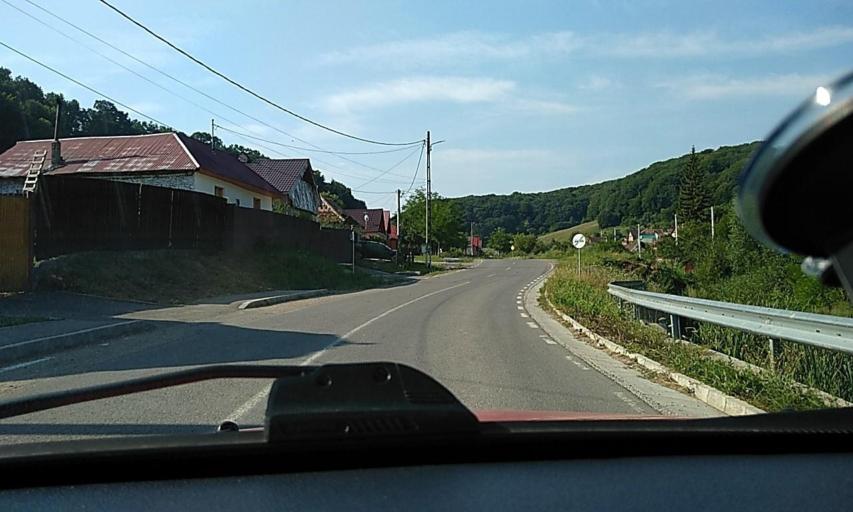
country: RO
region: Brasov
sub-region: Comuna Bunesti
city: Bunesti
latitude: 46.1027
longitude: 25.0591
